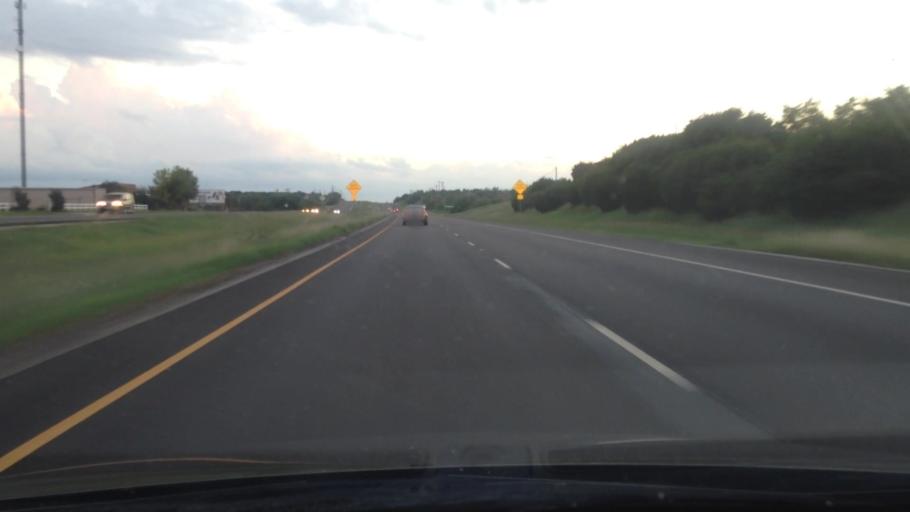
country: US
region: Texas
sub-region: Hood County
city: DeCordova
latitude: 32.5239
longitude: -97.6250
